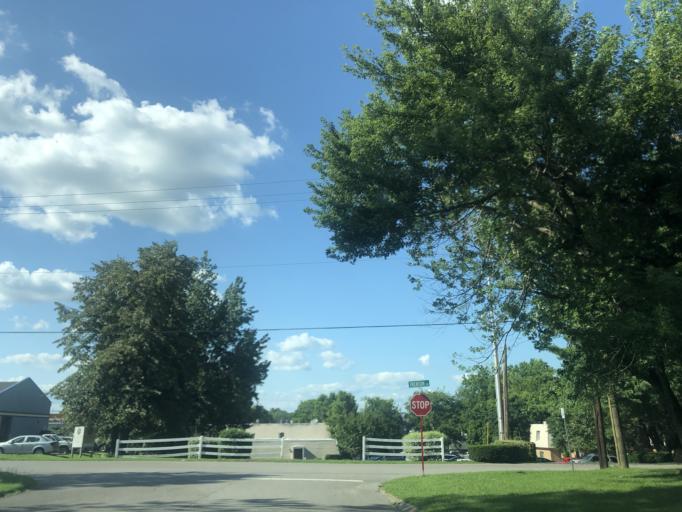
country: US
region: Tennessee
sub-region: Wilson County
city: Green Hill
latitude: 36.2132
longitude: -86.5966
